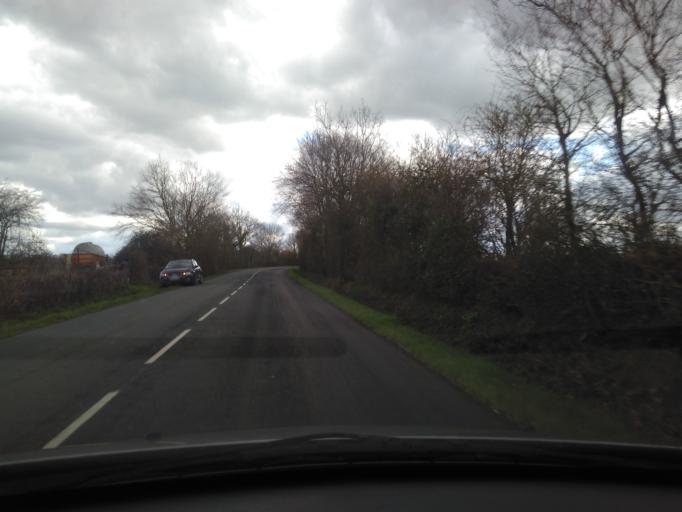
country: FR
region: Pays de la Loire
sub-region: Departement de la Vendee
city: Les Essarts
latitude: 46.7529
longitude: -1.2155
